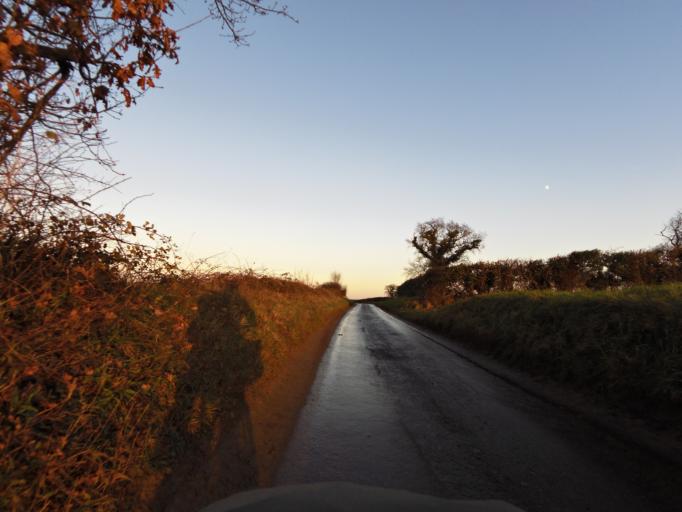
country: GB
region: England
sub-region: Norfolk
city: Aylsham
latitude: 52.8354
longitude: 1.1885
